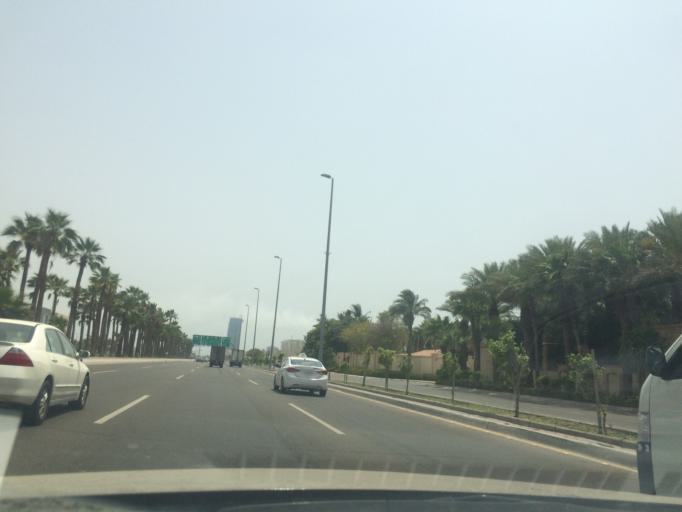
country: SA
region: Makkah
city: Jeddah
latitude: 21.5770
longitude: 39.1265
